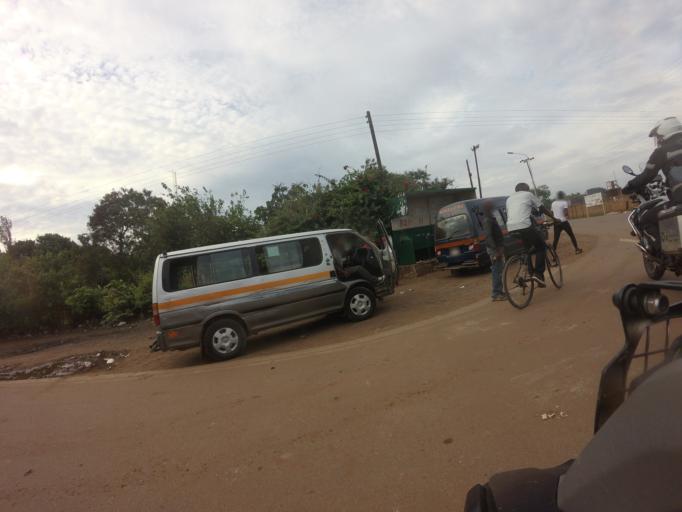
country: ZM
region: Lusaka
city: Lusaka
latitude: -15.5288
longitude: 28.2361
